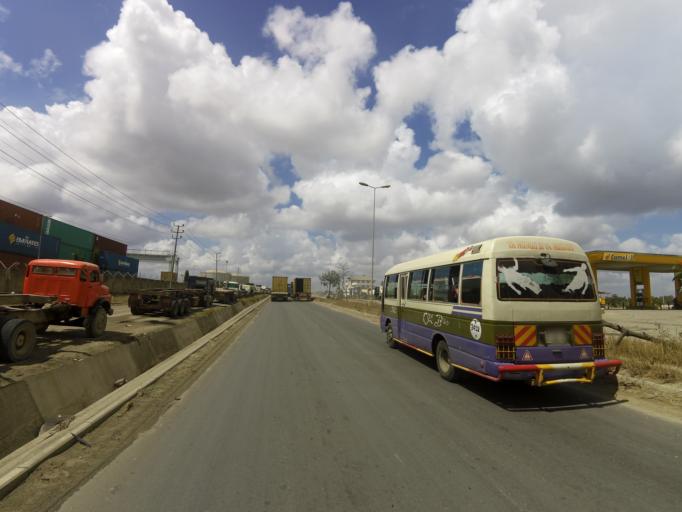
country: TZ
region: Dar es Salaam
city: Dar es Salaam
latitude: -6.8524
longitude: 39.2917
